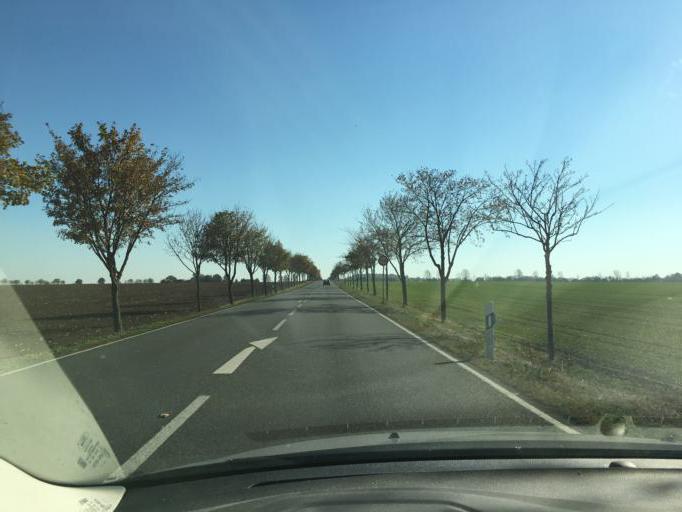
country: DE
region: Saxony-Anhalt
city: Wanzleben
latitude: 52.0471
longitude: 11.4569
